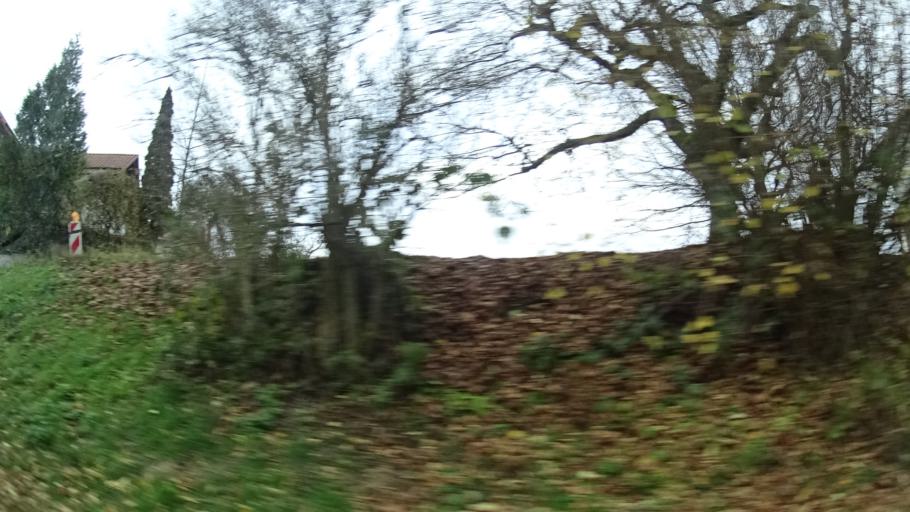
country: DE
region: Hesse
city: Hirschhorn
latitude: 49.4110
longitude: 8.9320
